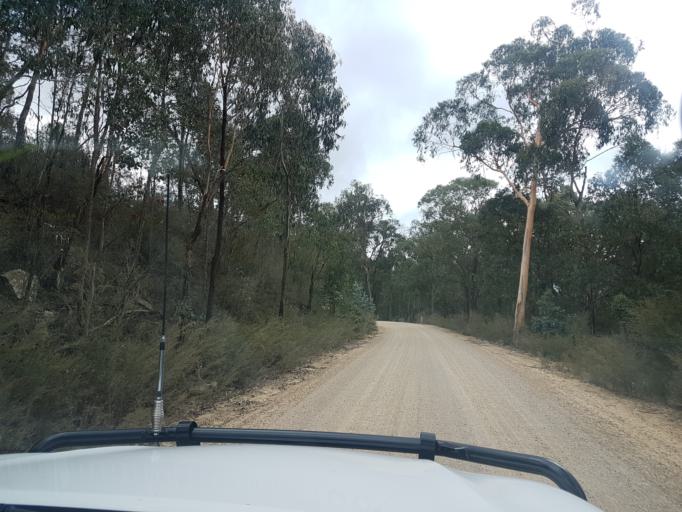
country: AU
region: Victoria
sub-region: East Gippsland
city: Bairnsdale
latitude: -37.6952
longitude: 147.5651
